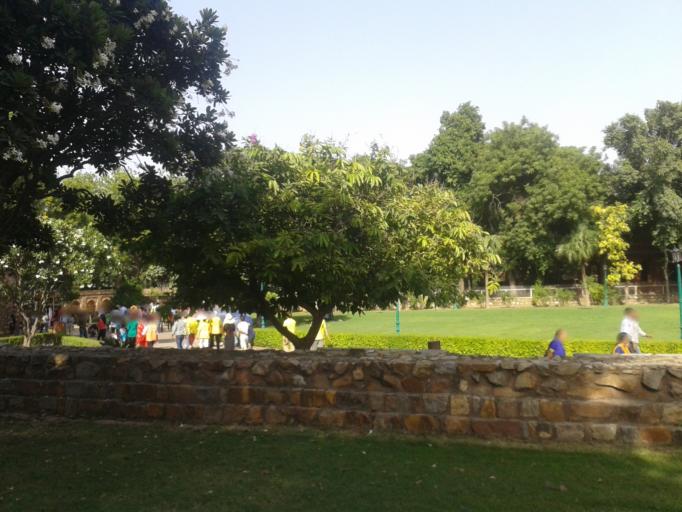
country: IN
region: NCT
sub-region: New Delhi
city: New Delhi
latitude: 28.5250
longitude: 77.1860
